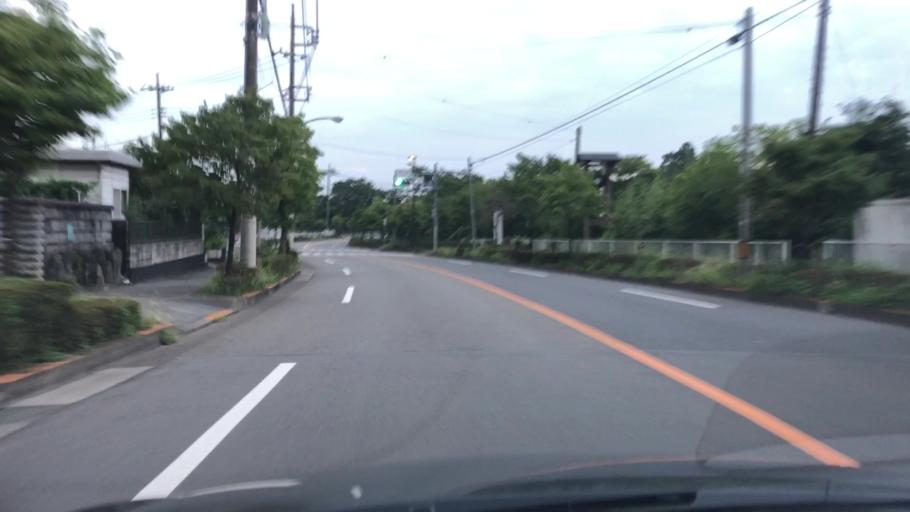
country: JP
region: Tokyo
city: Ome
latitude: 35.7414
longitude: 139.2627
